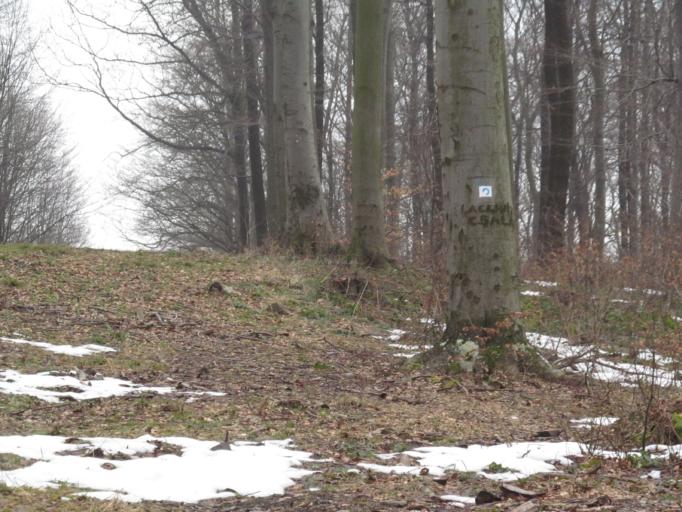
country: HU
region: Veszprem
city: Zirc
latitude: 47.2708
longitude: 17.8544
